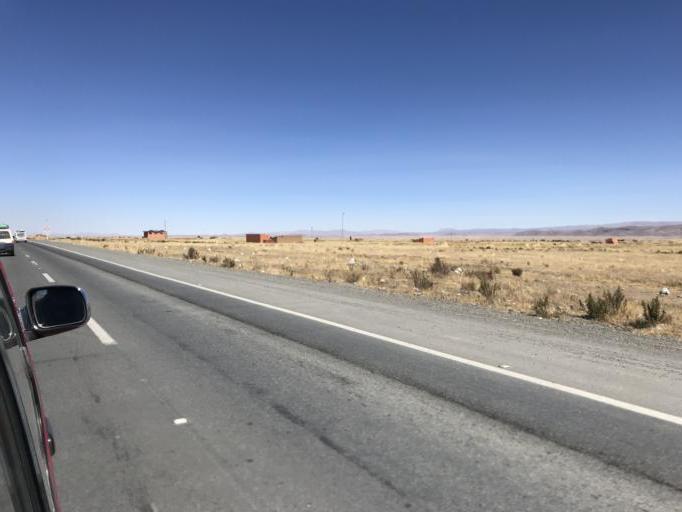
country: BO
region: La Paz
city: Batallas
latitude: -16.3581
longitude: -68.3971
